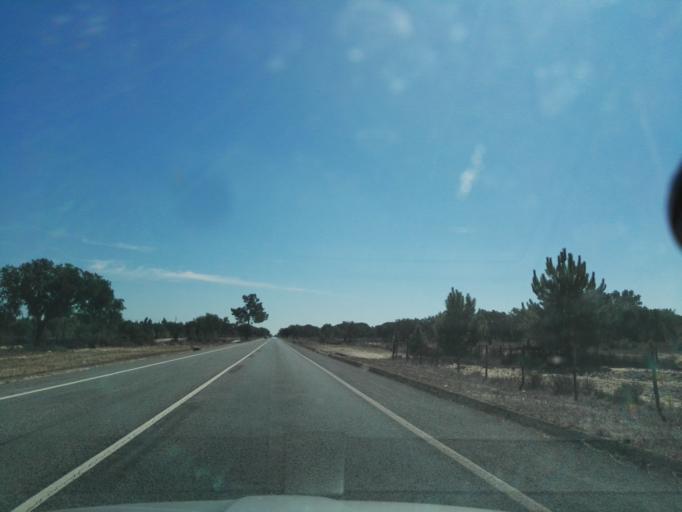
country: PT
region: Santarem
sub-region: Benavente
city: Samora Correia
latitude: 38.8894
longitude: -8.8276
